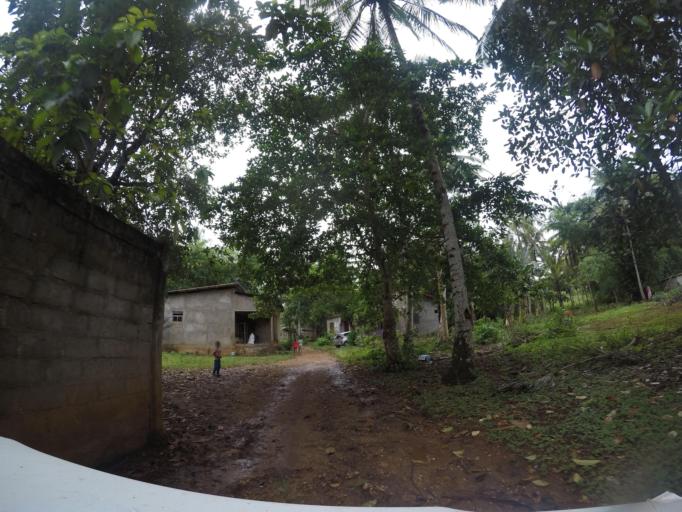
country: TL
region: Lautem
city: Lospalos
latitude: -8.5282
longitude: 126.9976
